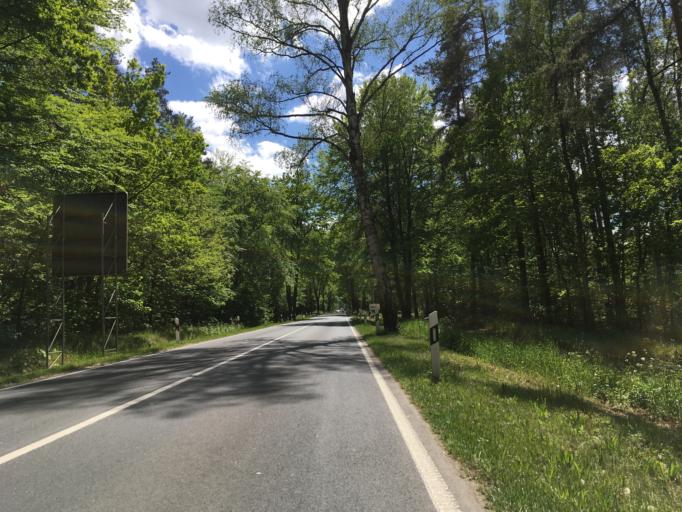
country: DE
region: Brandenburg
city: Rudnitz
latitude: 52.7696
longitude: 13.5648
